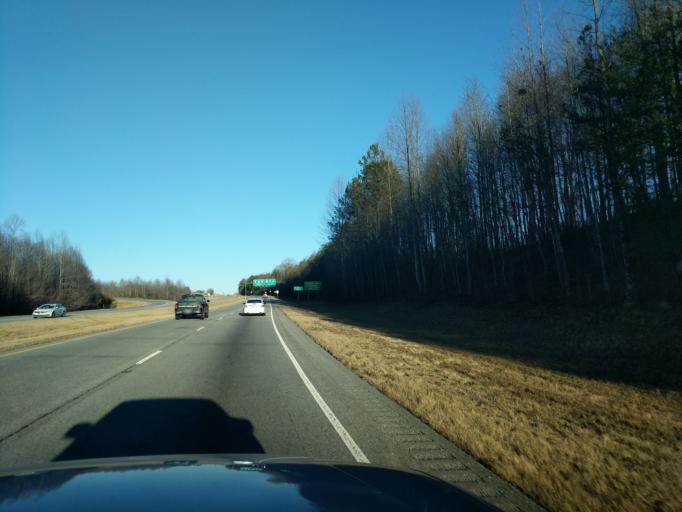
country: US
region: Georgia
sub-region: Habersham County
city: Clarkesville
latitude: 34.5896
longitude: -83.4481
